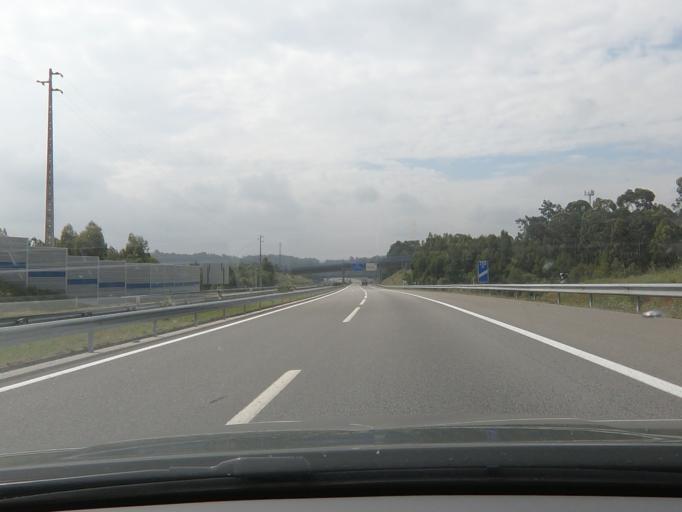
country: PT
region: Aveiro
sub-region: Aveiro
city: Oliveirinha
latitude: 40.6299
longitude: -8.6021
